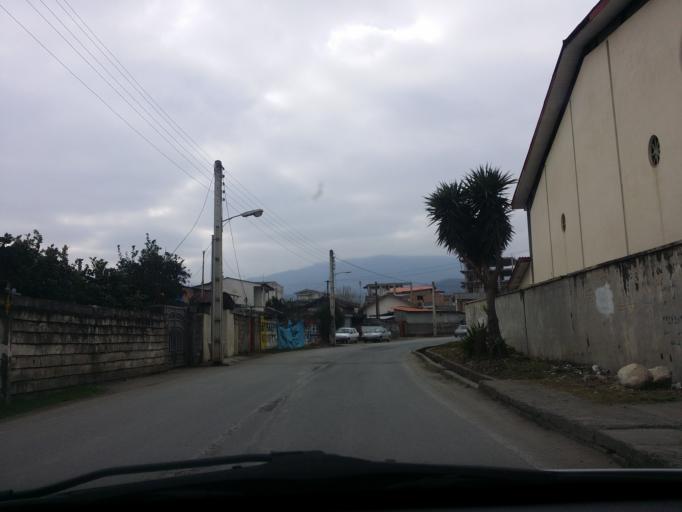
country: IR
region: Mazandaran
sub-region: Nowshahr
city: Nowshahr
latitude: 36.6452
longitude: 51.4816
